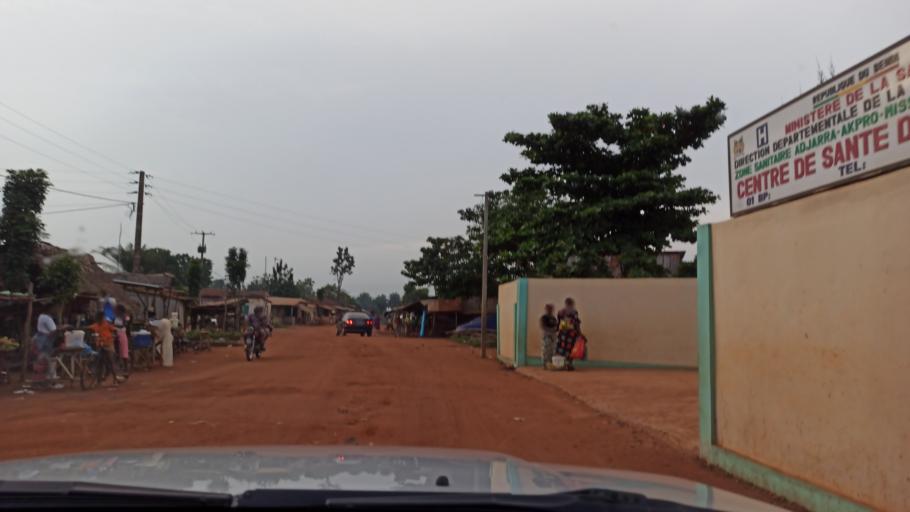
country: BJ
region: Queme
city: Porto-Novo
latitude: 6.5333
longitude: 2.6597
